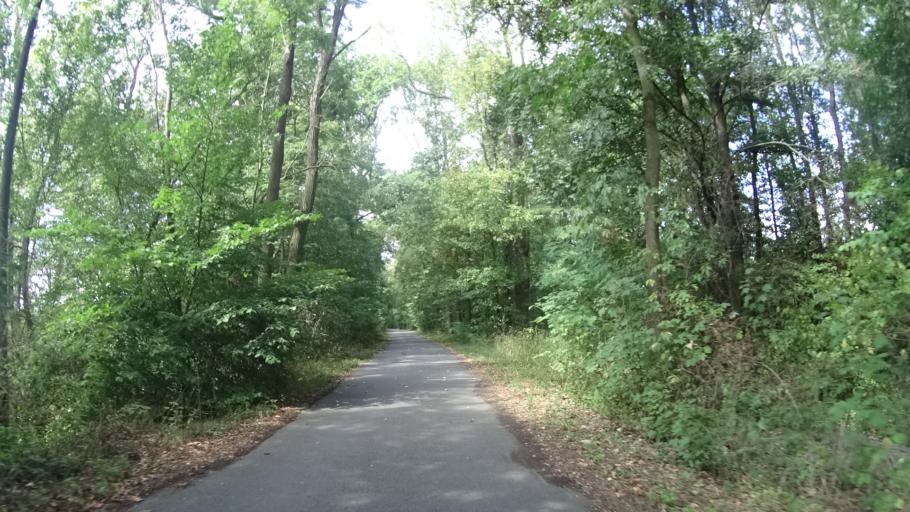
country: CZ
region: Olomoucky
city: Horka nad Moravou
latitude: 49.6498
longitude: 17.1954
